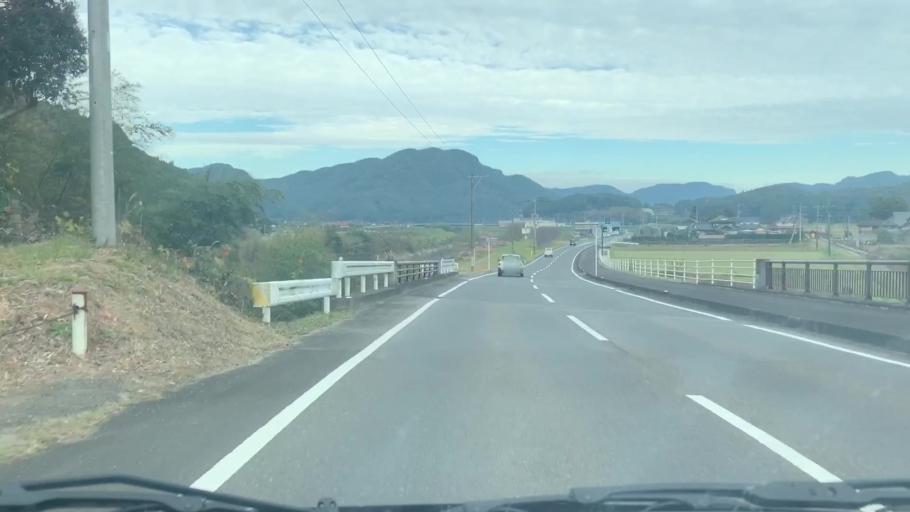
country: JP
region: Saga Prefecture
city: Imaricho-ko
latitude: 33.2924
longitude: 129.9700
